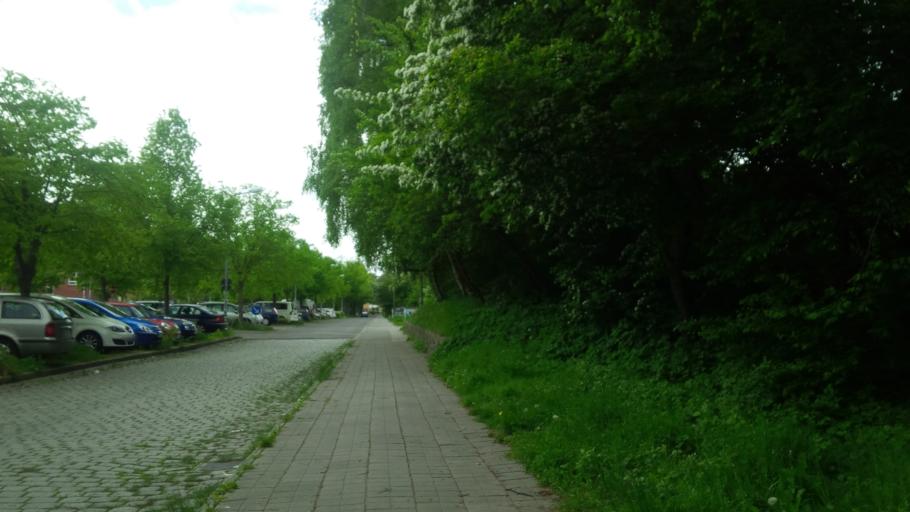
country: DE
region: Mecklenburg-Vorpommern
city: Rostock
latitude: 54.0905
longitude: 12.0973
